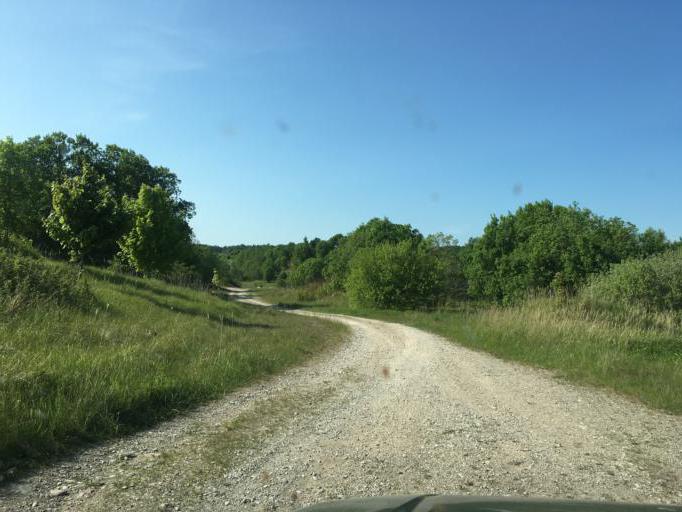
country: LV
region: Dundaga
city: Dundaga
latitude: 57.6101
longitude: 22.4422
